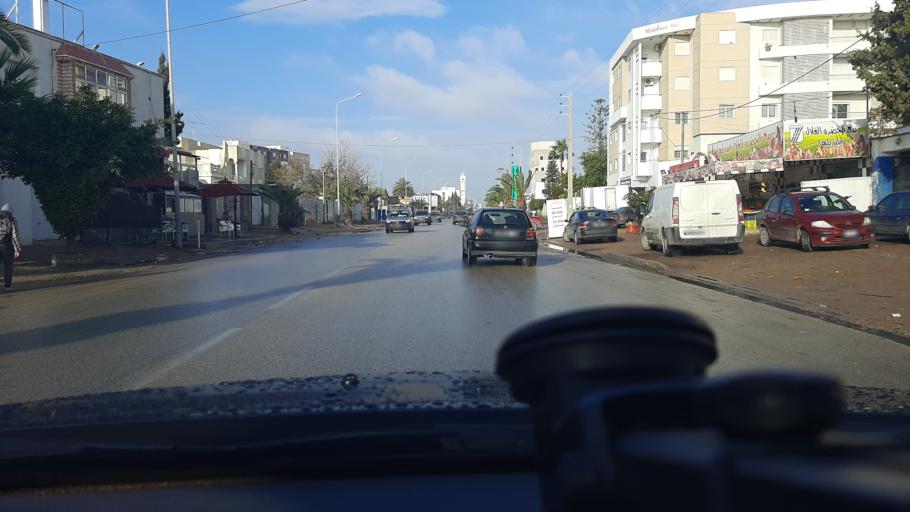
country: TN
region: Safaqis
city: Sfax
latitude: 34.7429
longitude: 10.7331
